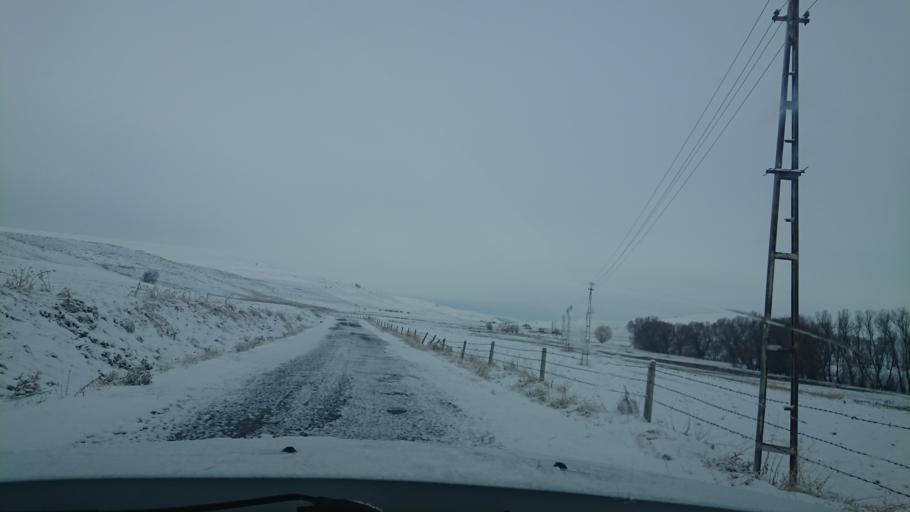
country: TR
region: Aksaray
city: Acipinar
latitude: 38.6795
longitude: 33.8658
